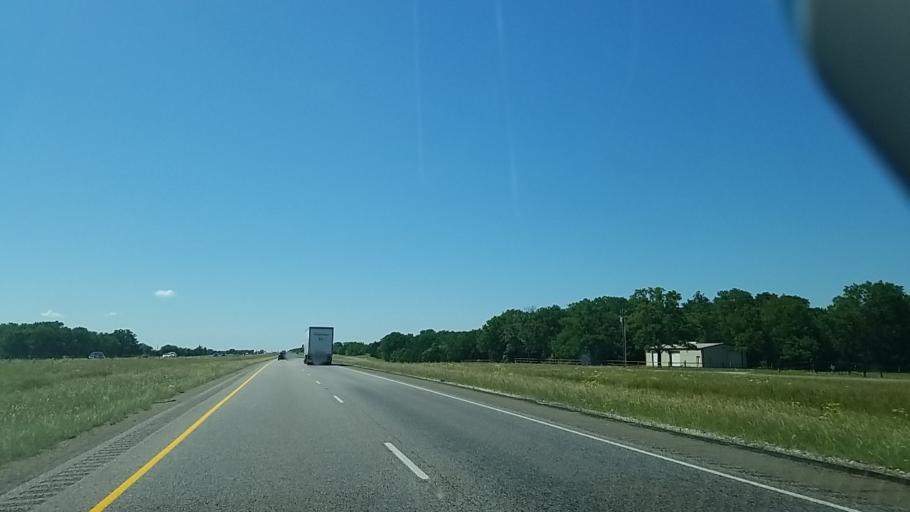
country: US
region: Texas
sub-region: Freestone County
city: Fairfield
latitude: 31.7637
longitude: -96.2125
